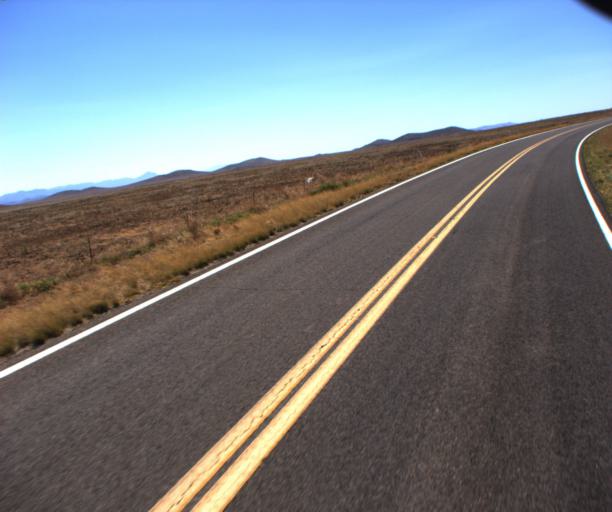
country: US
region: Arizona
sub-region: Cochise County
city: Douglas
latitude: 31.5569
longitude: -109.2656
